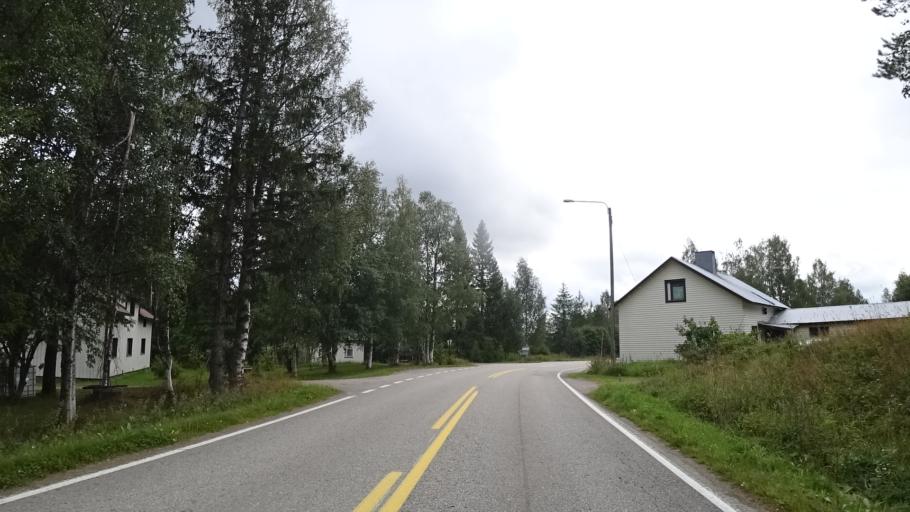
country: FI
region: North Karelia
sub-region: Joensuu
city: Ilomantsi
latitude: 62.9332
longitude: 31.2823
